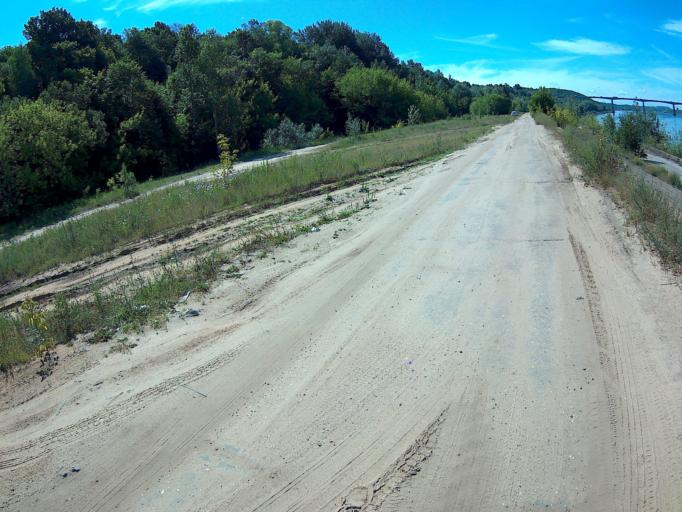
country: RU
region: Nizjnij Novgorod
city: Nizhniy Novgorod
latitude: 56.2598
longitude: 43.9663
